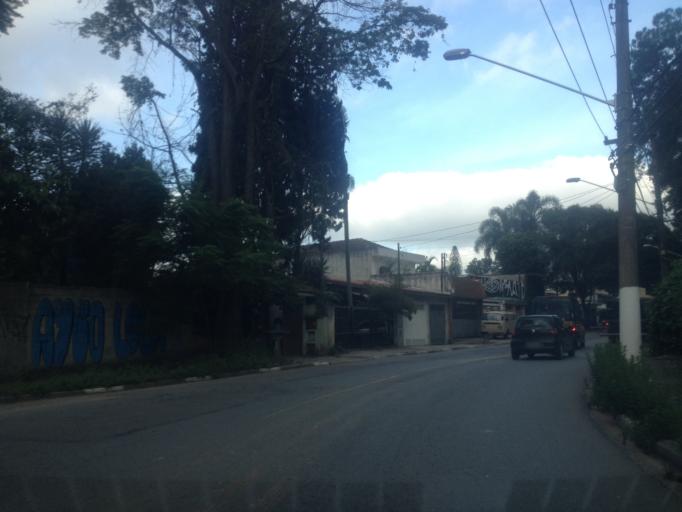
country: BR
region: Sao Paulo
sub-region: Diadema
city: Diadema
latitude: -23.7267
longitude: -46.7176
